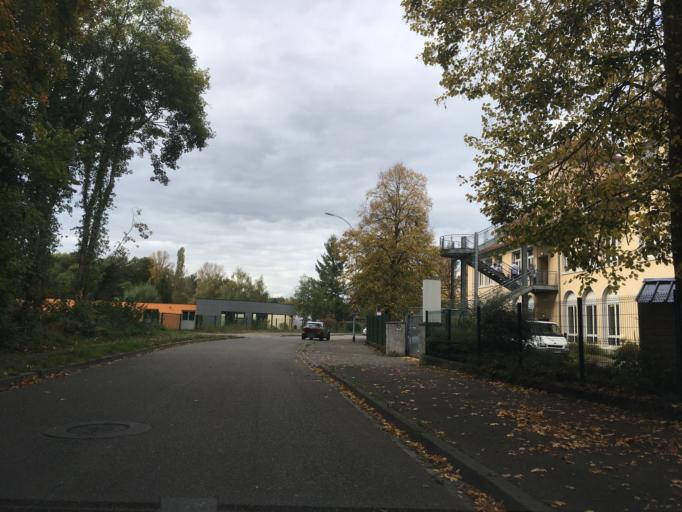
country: FR
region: Alsace
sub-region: Departement du Bas-Rhin
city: Illkirch-Graffenstaden
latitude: 48.5331
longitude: 7.7609
